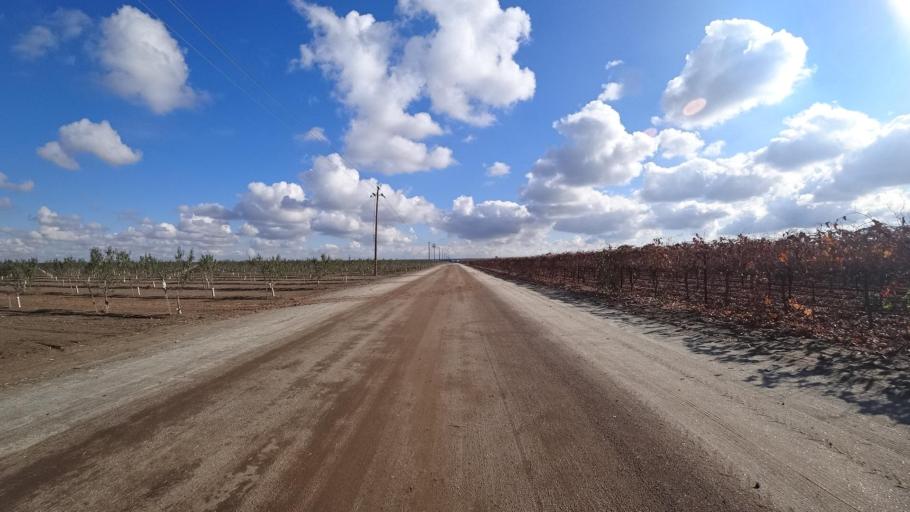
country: US
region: California
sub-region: Kern County
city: McFarland
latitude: 35.6527
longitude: -119.2297
